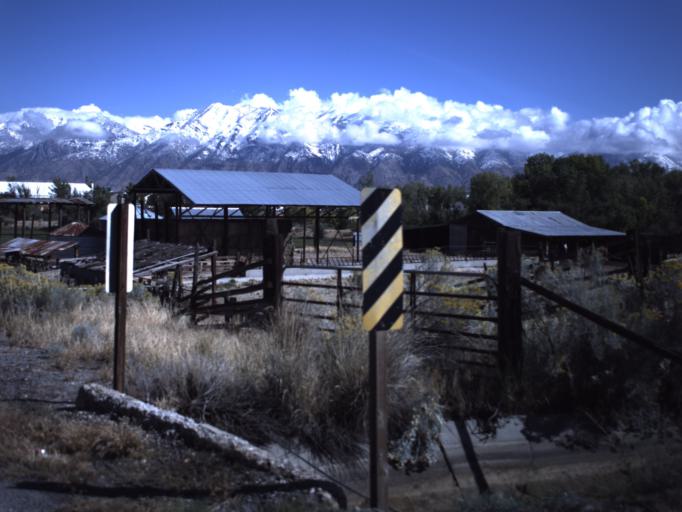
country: US
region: Utah
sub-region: Utah County
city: Spanish Fork
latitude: 40.0994
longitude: -111.6807
